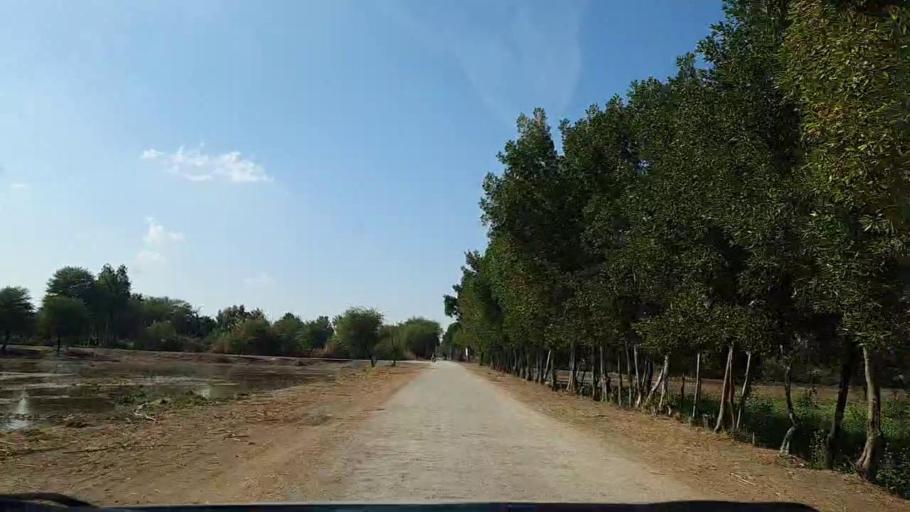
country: PK
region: Sindh
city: Pithoro
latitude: 25.6664
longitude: 69.4535
